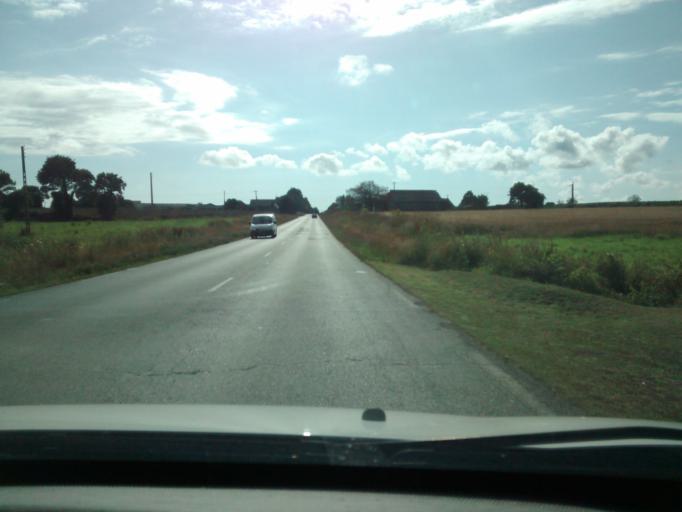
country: FR
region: Brittany
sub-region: Departement des Cotes-d'Armor
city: Rospez
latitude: 48.7445
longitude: -3.3842
